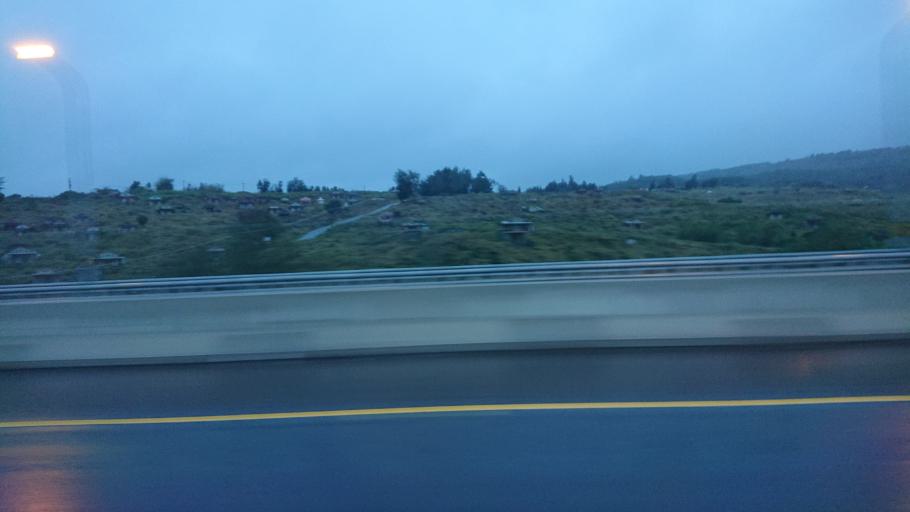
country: TW
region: Taiwan
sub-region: Miaoli
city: Miaoli
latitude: 24.5672
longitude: 120.7143
